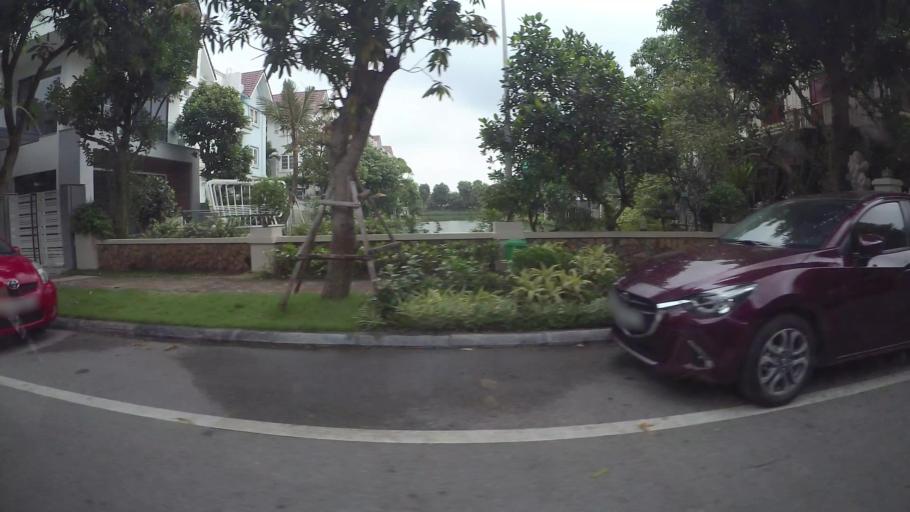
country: VN
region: Ha Noi
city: Trau Quy
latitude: 21.0423
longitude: 105.9208
